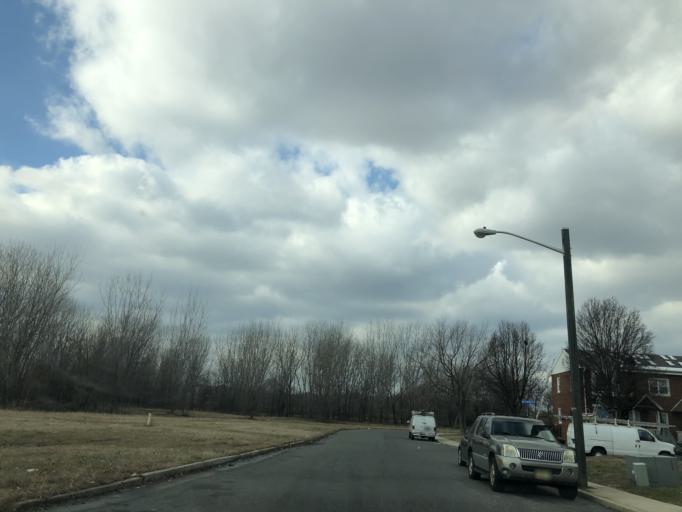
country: US
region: New Jersey
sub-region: Camden County
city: Wood-Lynne
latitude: 39.9408
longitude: -75.0935
